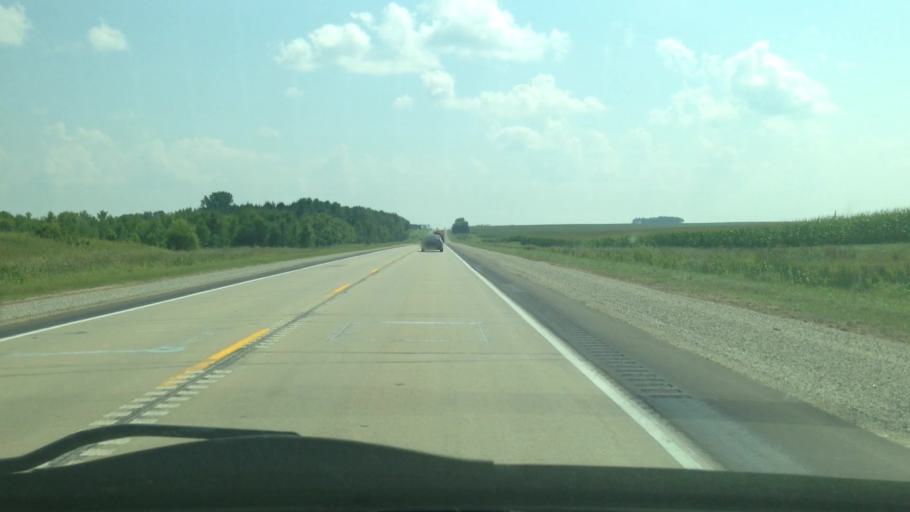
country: US
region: Iowa
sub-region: Howard County
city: Cresco
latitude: 43.3925
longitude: -92.2983
